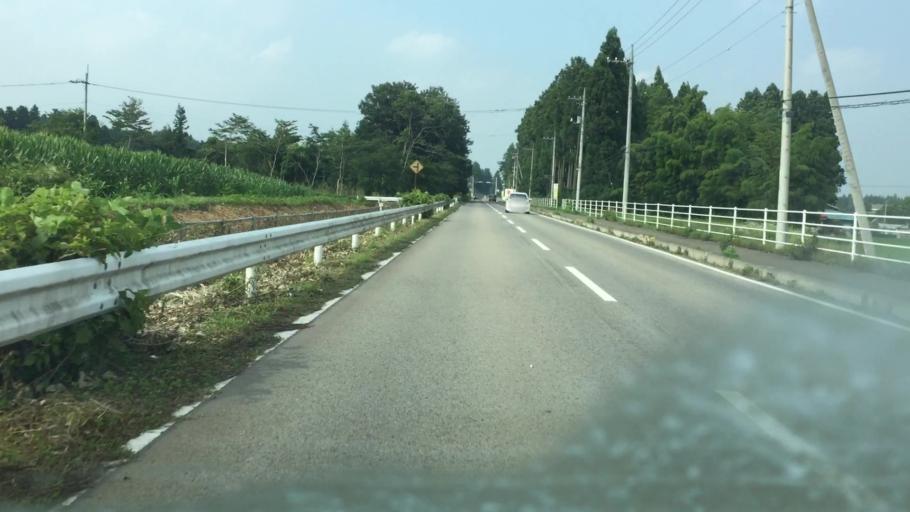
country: JP
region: Tochigi
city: Kuroiso
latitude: 36.9827
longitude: 139.9841
